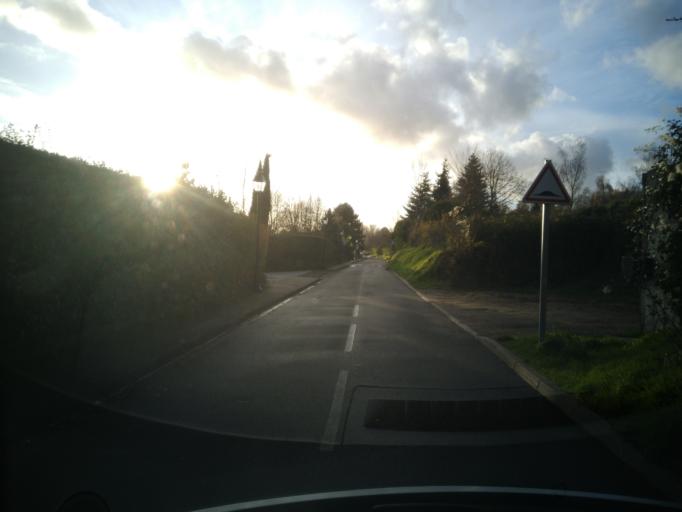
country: FR
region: Ile-de-France
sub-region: Departement des Yvelines
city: Chambourcy
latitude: 48.8979
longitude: 2.0377
